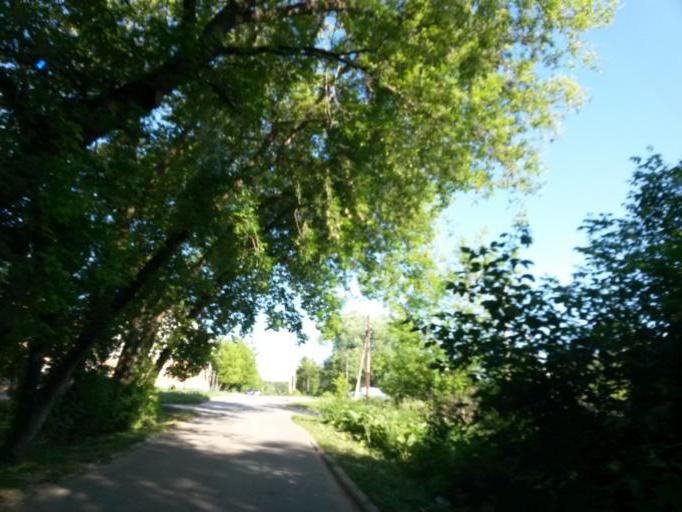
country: RU
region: Moskovskaya
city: Lyubuchany
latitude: 55.2397
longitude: 37.5383
